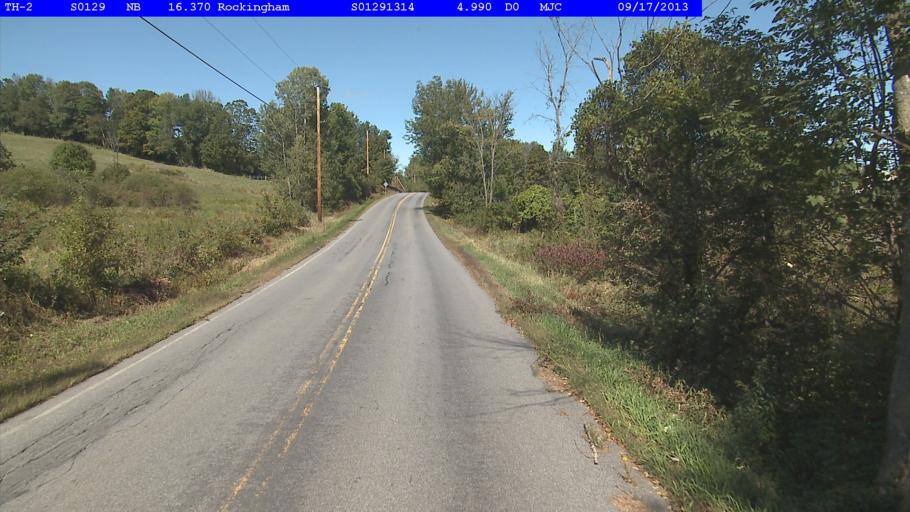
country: US
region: Vermont
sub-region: Windham County
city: Rockingham
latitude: 43.1882
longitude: -72.5117
